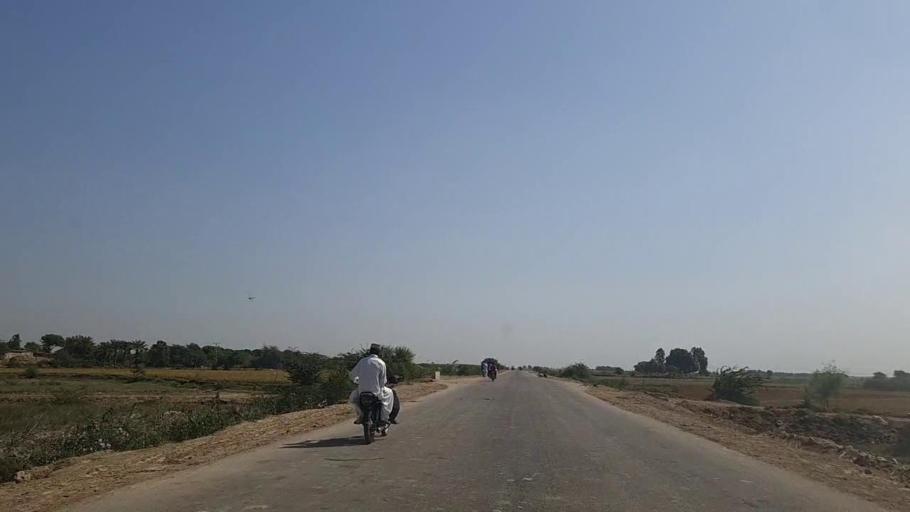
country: PK
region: Sindh
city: Mirpur Batoro
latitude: 24.7577
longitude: 68.2256
